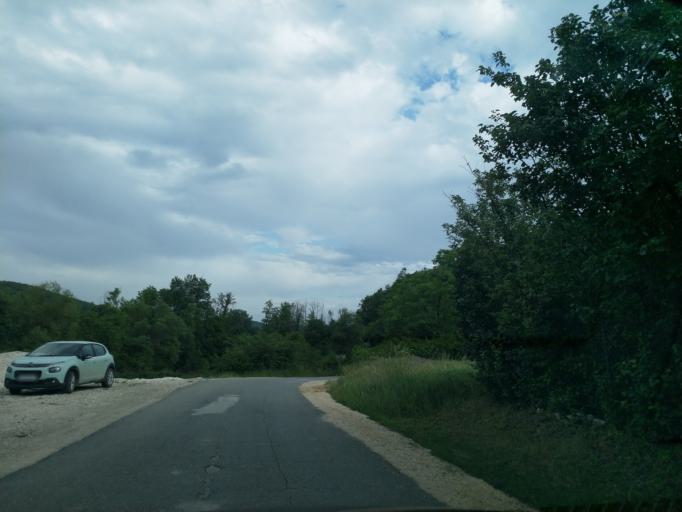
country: RS
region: Central Serbia
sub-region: Borski Okrug
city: Bor
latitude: 44.0259
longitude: 21.9765
